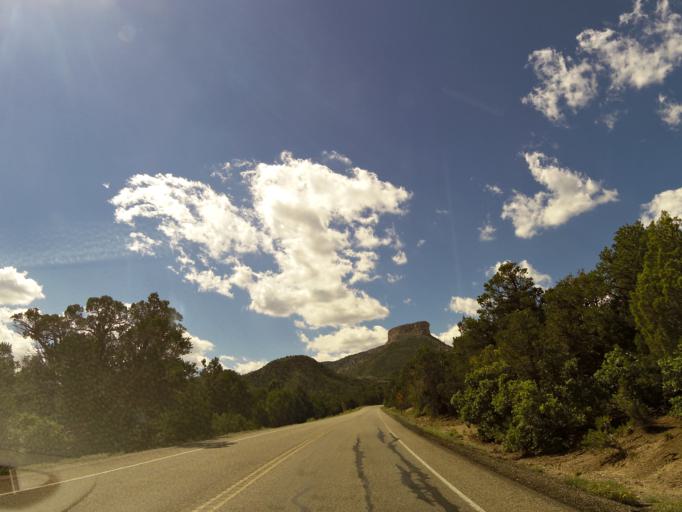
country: US
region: Colorado
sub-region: Montezuma County
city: Mancos
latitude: 37.3364
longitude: -108.4116
